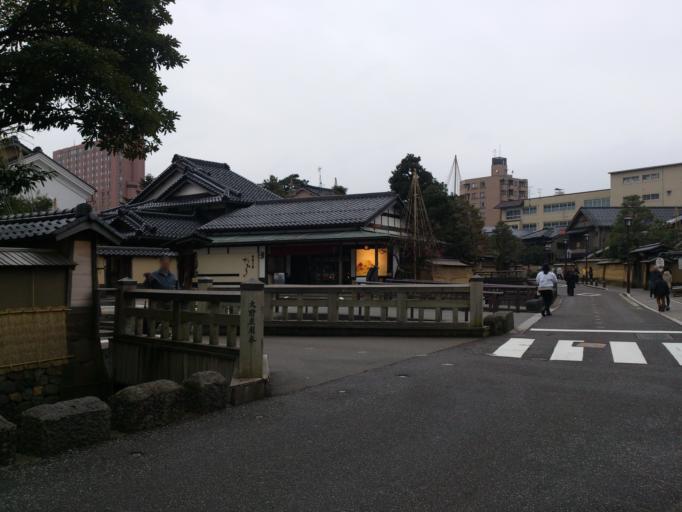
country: JP
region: Ishikawa
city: Kanazawa-shi
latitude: 36.5644
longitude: 136.6497
